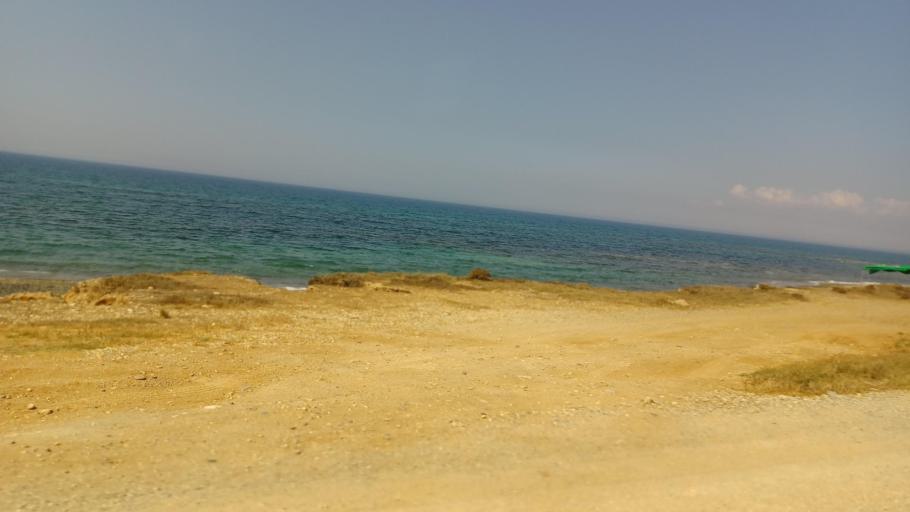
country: CY
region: Larnaka
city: Xylotymbou
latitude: 34.9761
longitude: 33.7919
